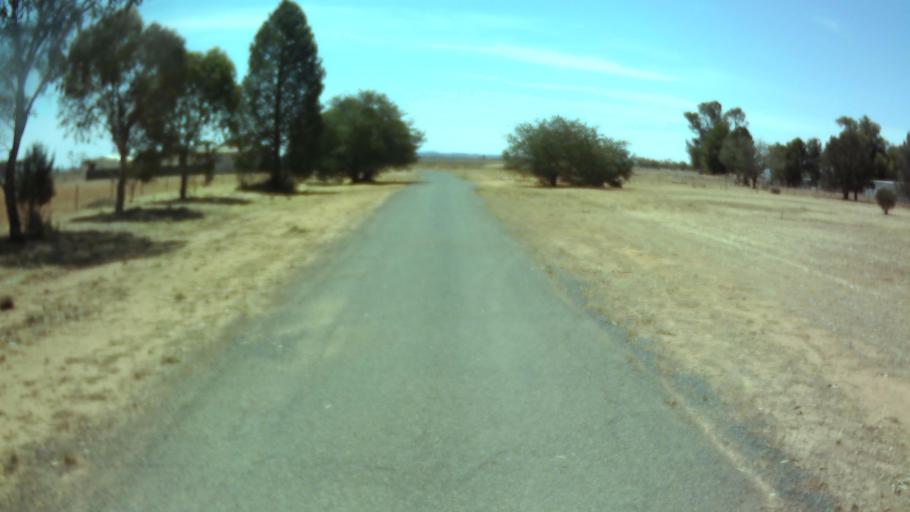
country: AU
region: New South Wales
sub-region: Weddin
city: Grenfell
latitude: -33.8408
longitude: 147.7396
